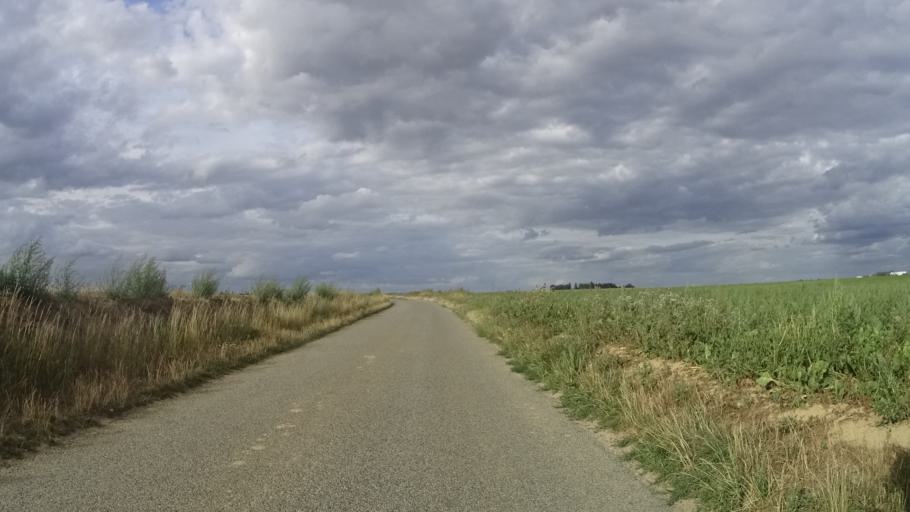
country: FR
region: Picardie
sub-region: Departement de l'Oise
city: Ver-sur-Launette
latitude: 49.0985
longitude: 2.7141
